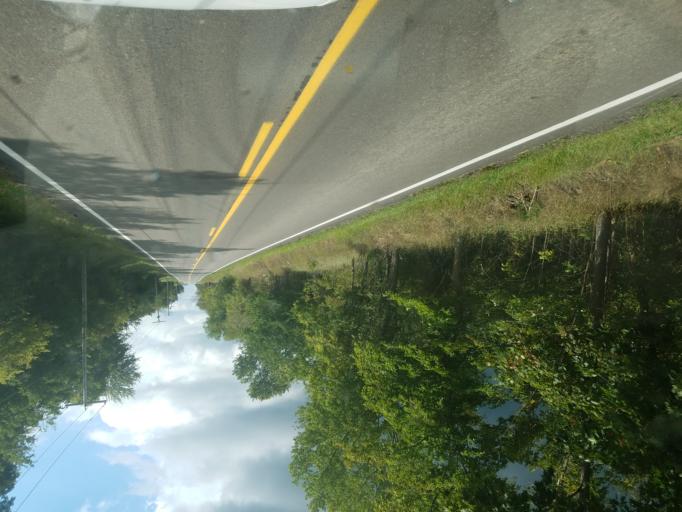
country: US
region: Ohio
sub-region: Huron County
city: Greenwich
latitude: 40.9240
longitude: -82.5254
